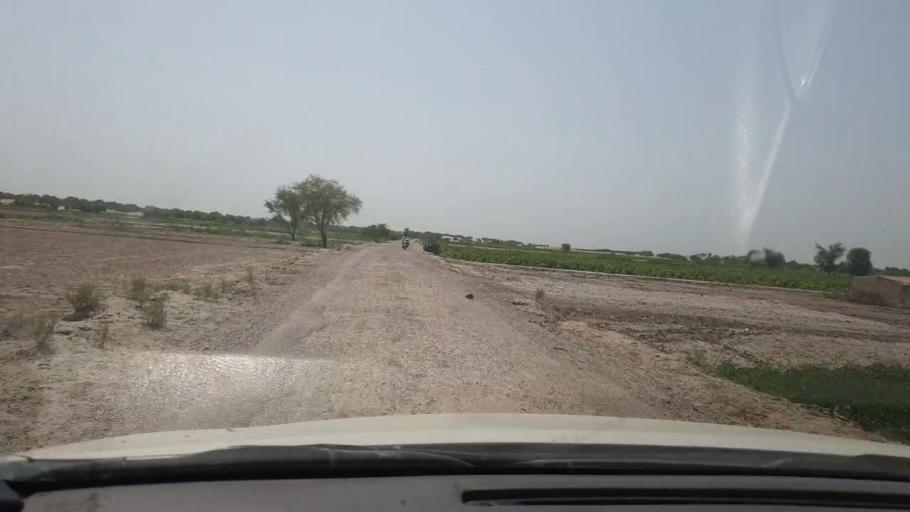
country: PK
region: Sindh
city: Rohri
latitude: 27.5185
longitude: 69.0828
